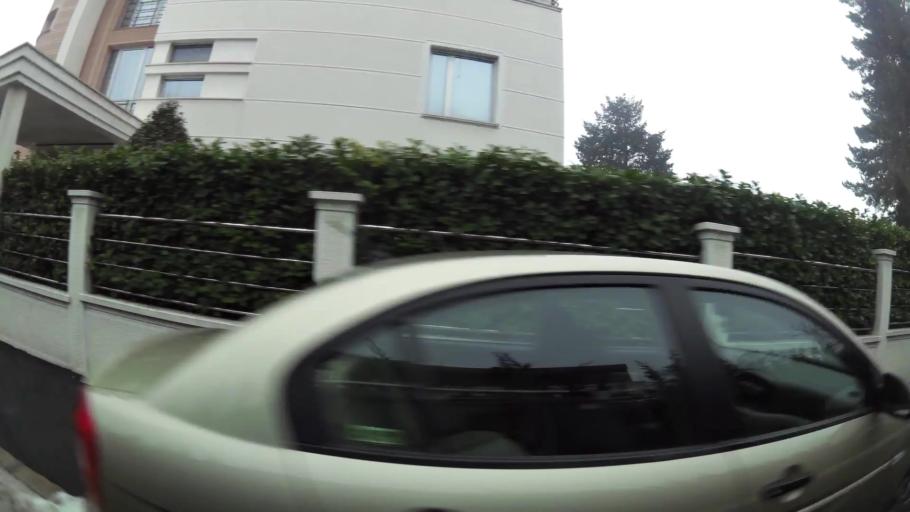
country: RS
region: Central Serbia
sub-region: Belgrade
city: Savski Venac
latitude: 44.7796
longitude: 20.4641
